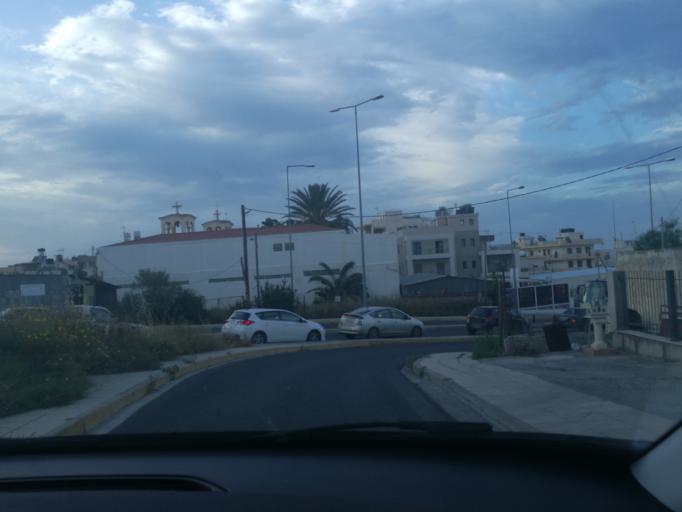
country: GR
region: Crete
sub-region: Nomos Irakleiou
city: Irakleion
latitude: 35.3212
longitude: 25.1408
